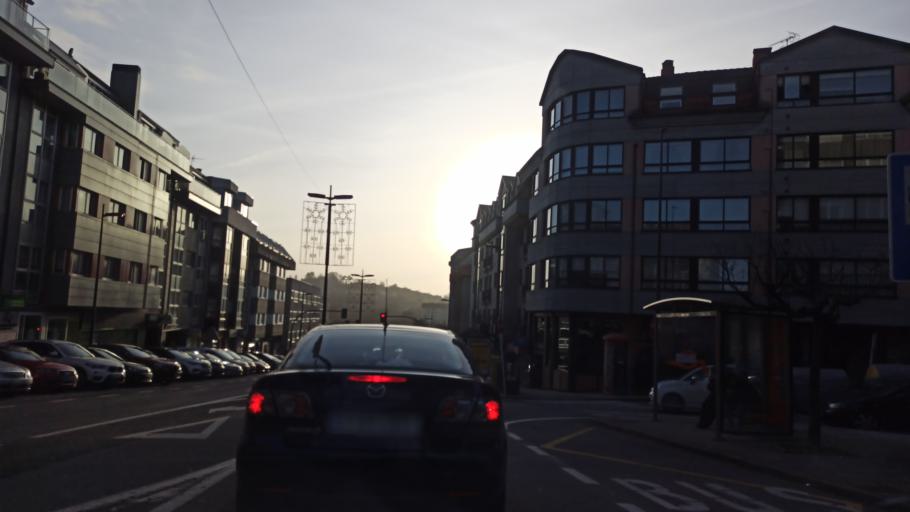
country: ES
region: Galicia
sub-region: Provincia da Coruna
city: Cambre
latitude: 43.3182
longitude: -8.3564
